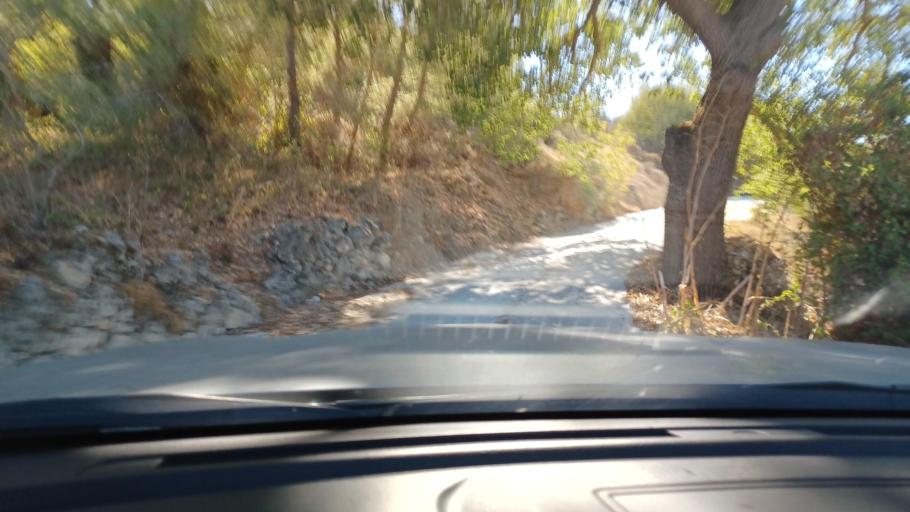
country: CY
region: Pafos
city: Polis
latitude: 35.0010
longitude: 32.5120
